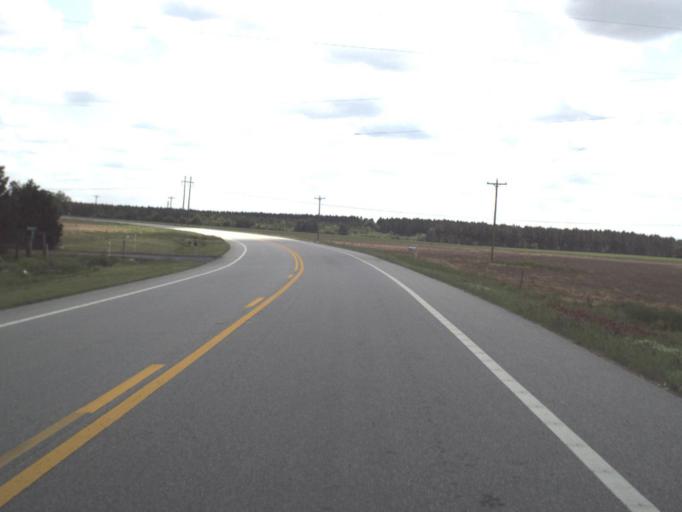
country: US
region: Alabama
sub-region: Escambia County
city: Atmore
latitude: 30.9343
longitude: -87.4880
